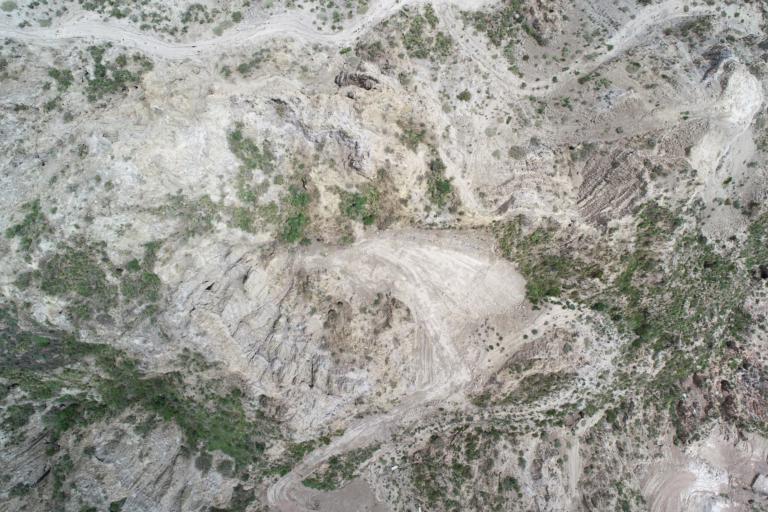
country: BO
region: La Paz
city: La Paz
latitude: -16.5429
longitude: -68.1176
